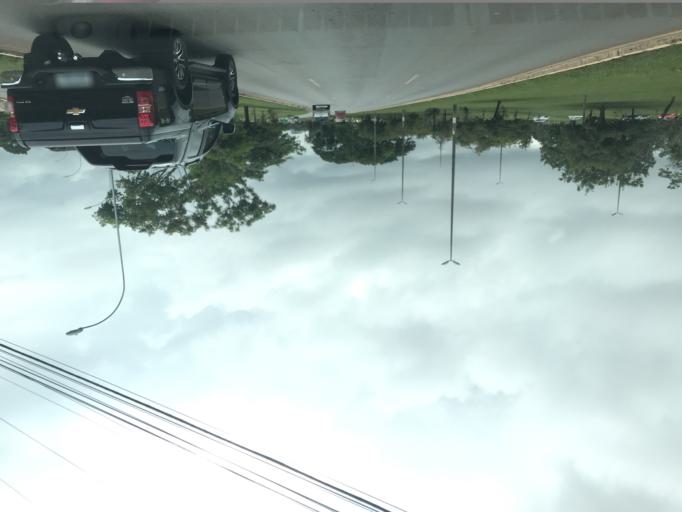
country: BR
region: Federal District
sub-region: Brasilia
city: Brasilia
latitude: -15.8211
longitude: -47.8826
